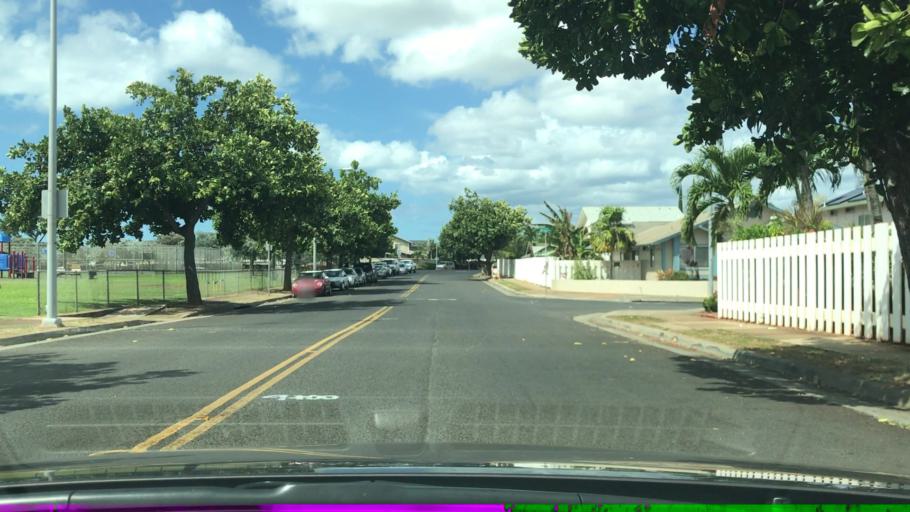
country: US
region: Hawaii
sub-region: Honolulu County
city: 'Ewa Gentry
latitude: 21.3346
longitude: -158.0276
